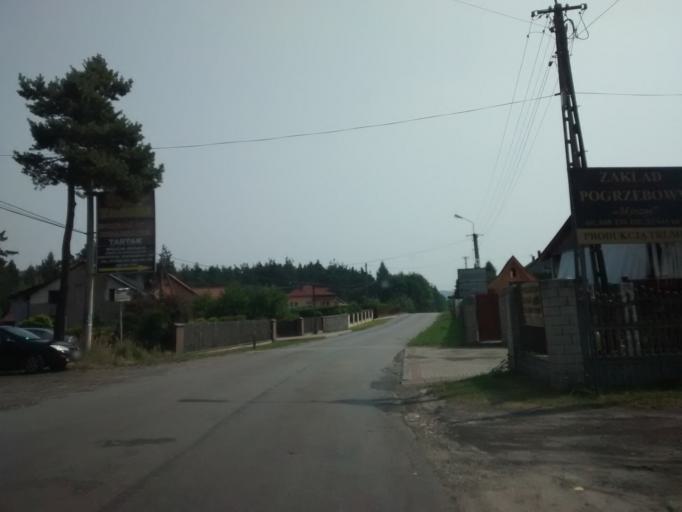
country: PL
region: Lesser Poland Voivodeship
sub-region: Powiat olkuski
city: Klucze
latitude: 50.3649
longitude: 19.5449
